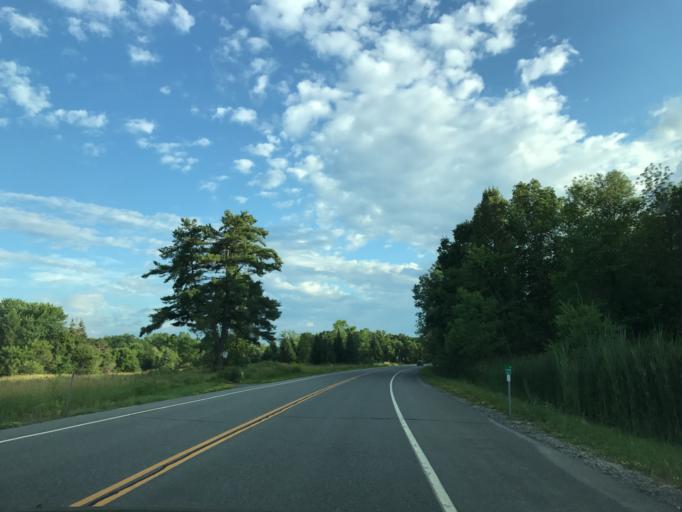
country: US
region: New York
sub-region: Saratoga County
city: Schuylerville
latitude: 43.0131
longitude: -73.5987
